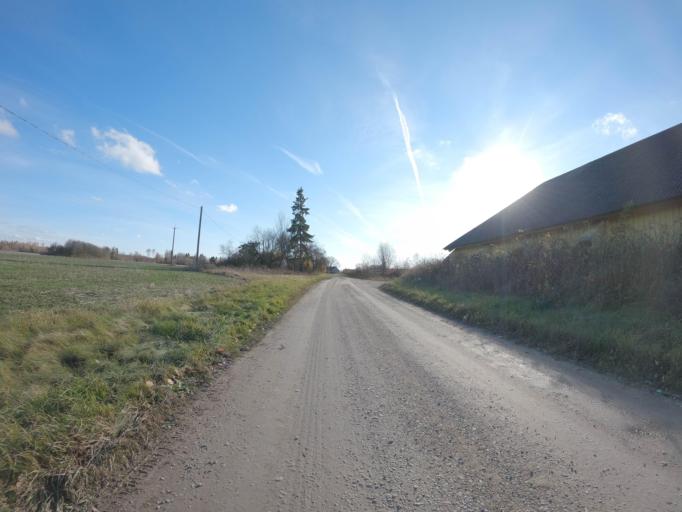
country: EE
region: Raplamaa
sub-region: Rapla vald
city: Rapla
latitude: 59.0273
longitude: 24.7938
